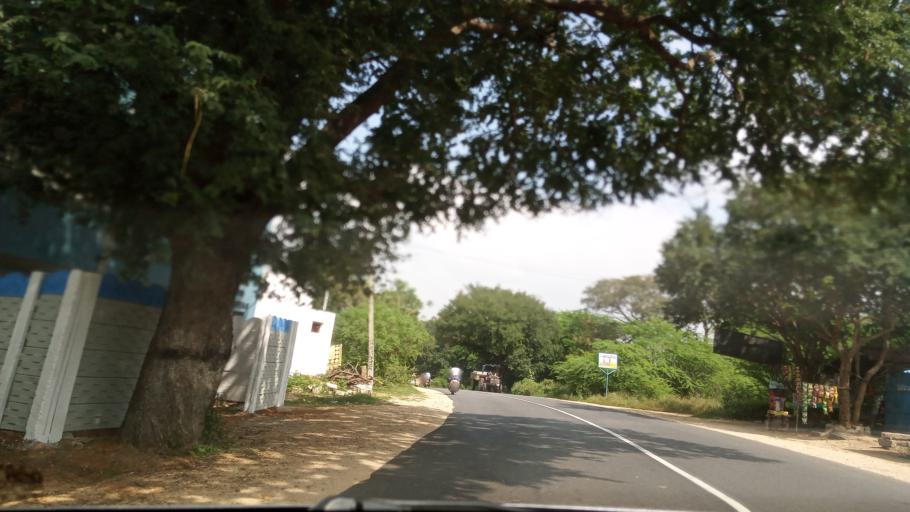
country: IN
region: Andhra Pradesh
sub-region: Chittoor
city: Madanapalle
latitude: 13.6026
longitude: 78.5346
